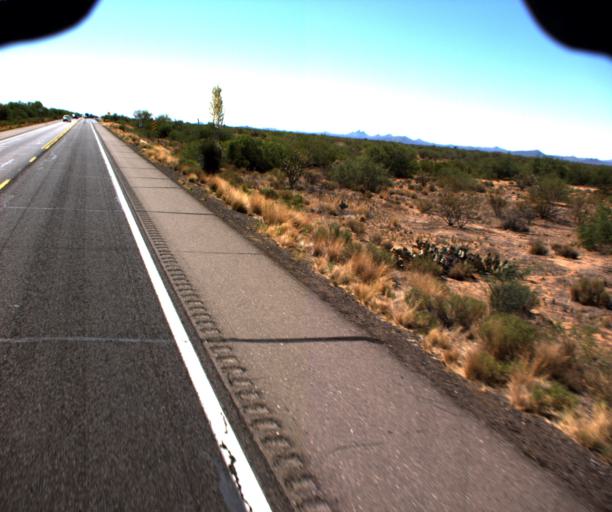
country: US
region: Arizona
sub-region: Yavapai County
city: Congress
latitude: 34.1051
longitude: -112.9242
